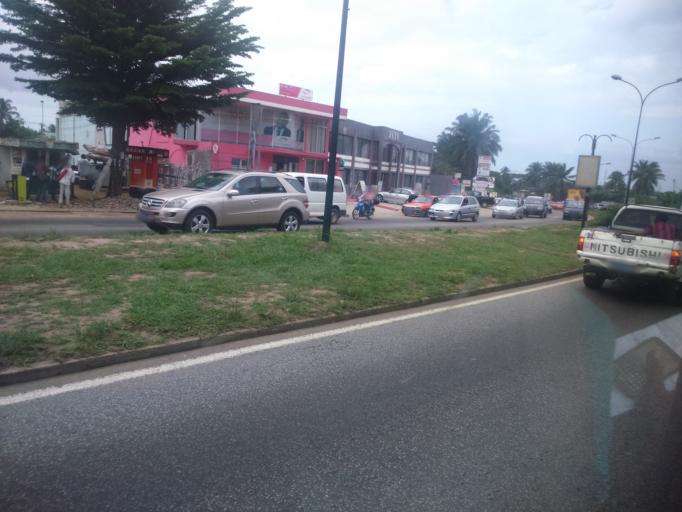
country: CI
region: Lagunes
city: Abidjan
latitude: 5.3585
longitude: -4.0008
